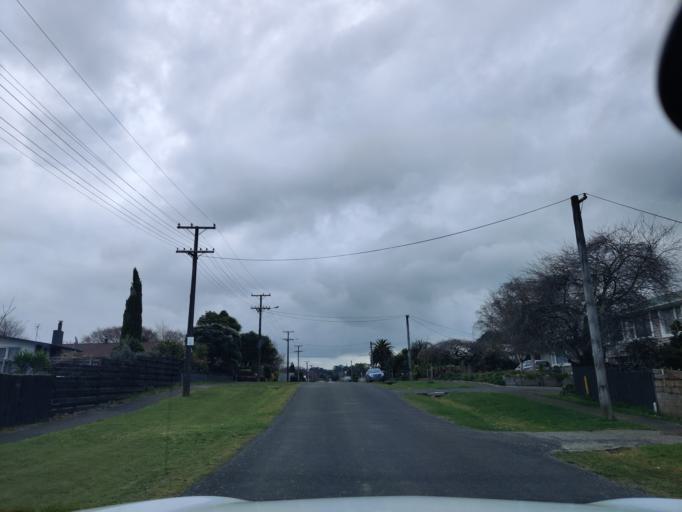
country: NZ
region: Manawatu-Wanganui
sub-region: Palmerston North City
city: Palmerston North
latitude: -40.2895
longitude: 175.7598
